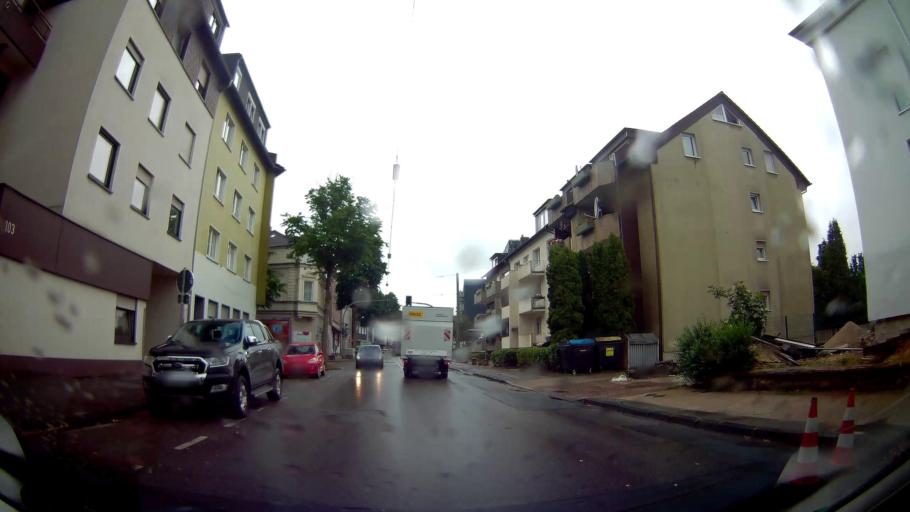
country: DE
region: North Rhine-Westphalia
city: Bochum-Hordel
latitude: 51.4969
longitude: 7.1492
